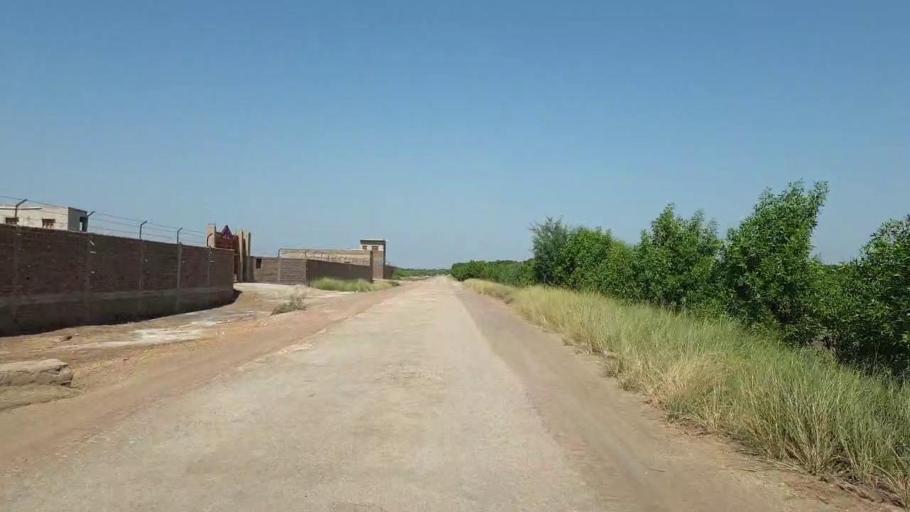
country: PK
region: Sindh
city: Tando Jam
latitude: 25.4106
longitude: 68.4548
